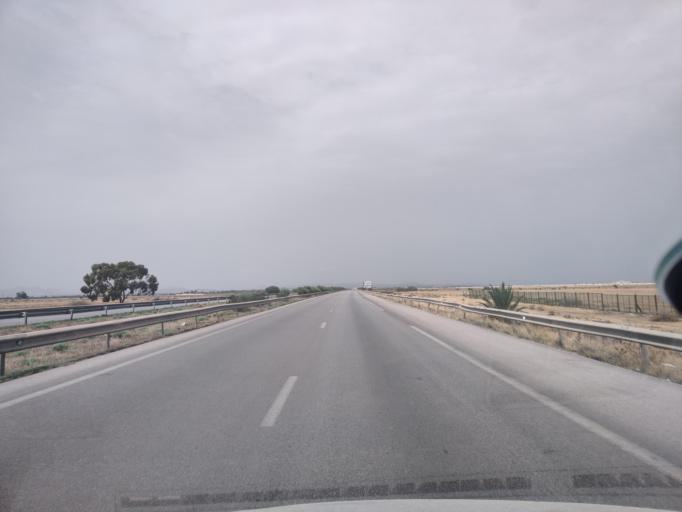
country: TN
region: Susah
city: Harqalah
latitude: 36.0600
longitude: 10.4089
